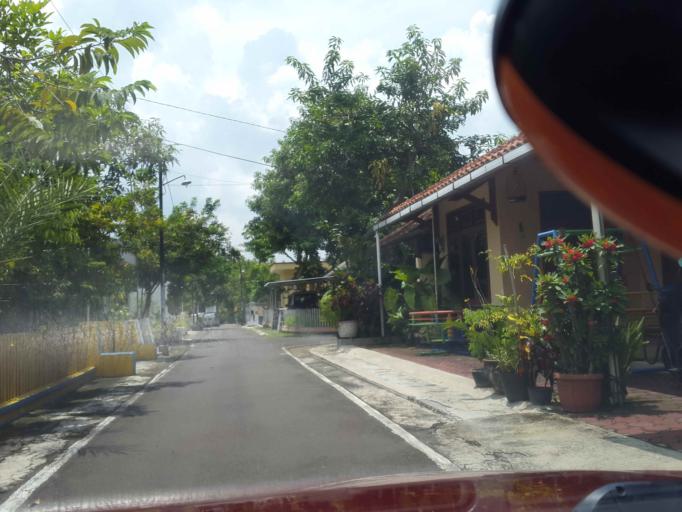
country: ID
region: Central Java
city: Jaten
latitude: -7.6074
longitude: 110.9766
